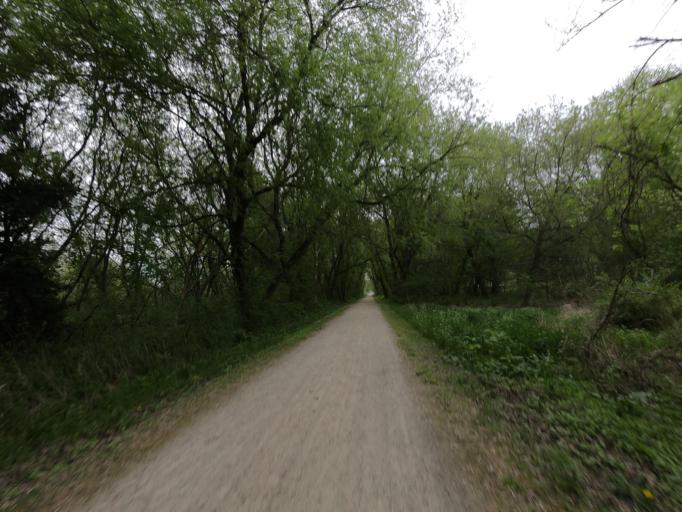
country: US
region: Wisconsin
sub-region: Jefferson County
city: Lake Mills
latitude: 43.0464
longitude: -88.8604
